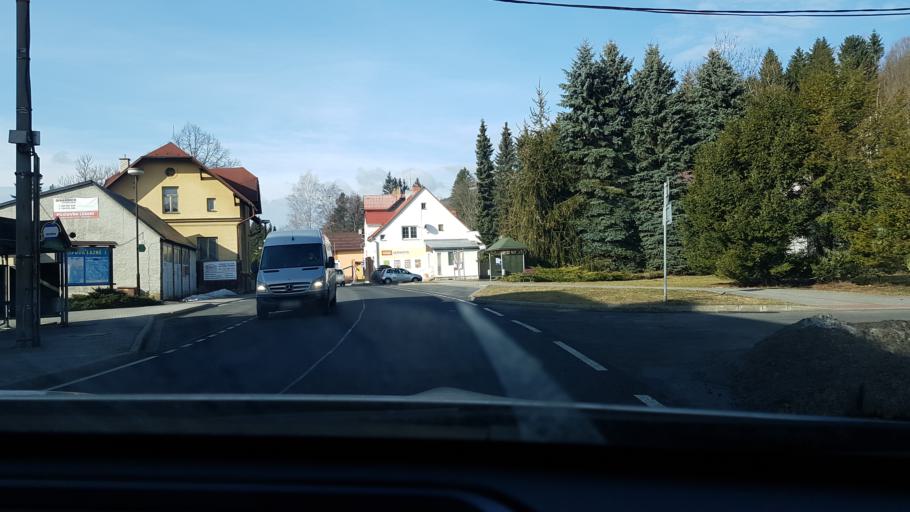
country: CZ
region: Olomoucky
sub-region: Okres Jesenik
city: Jesenik
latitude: 50.2291
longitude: 17.1478
